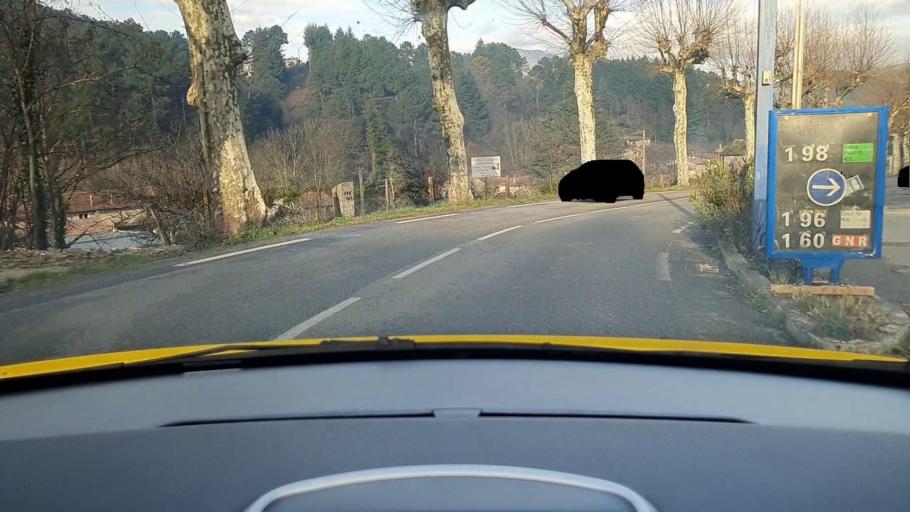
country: FR
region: Languedoc-Roussillon
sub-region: Departement du Gard
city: Branoux-les-Taillades
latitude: 44.2988
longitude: 3.9781
